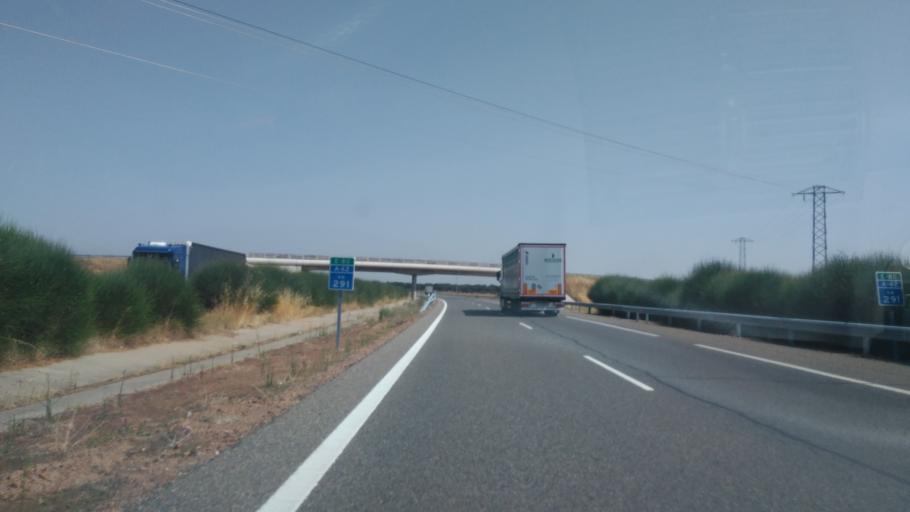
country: ES
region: Castille and Leon
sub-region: Provincia de Salamanca
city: La Fuente de San Esteban
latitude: 40.7945
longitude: -6.2144
